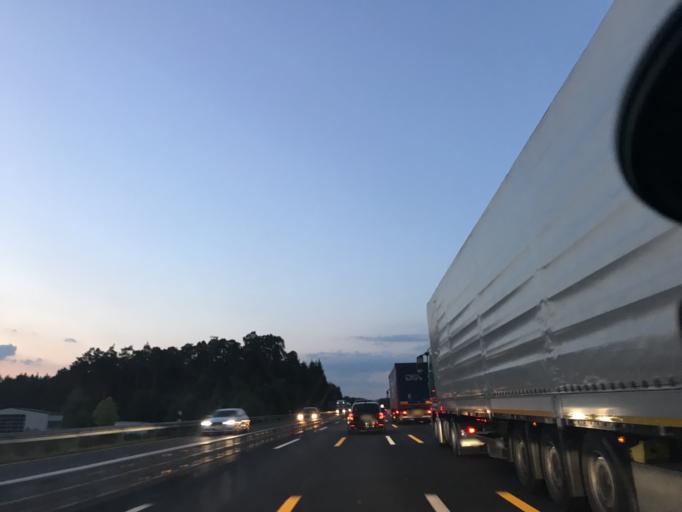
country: DE
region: Bavaria
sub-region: Regierungsbezirk Mittelfranken
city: Neunkirchen am Sand
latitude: 49.5361
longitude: 11.3182
